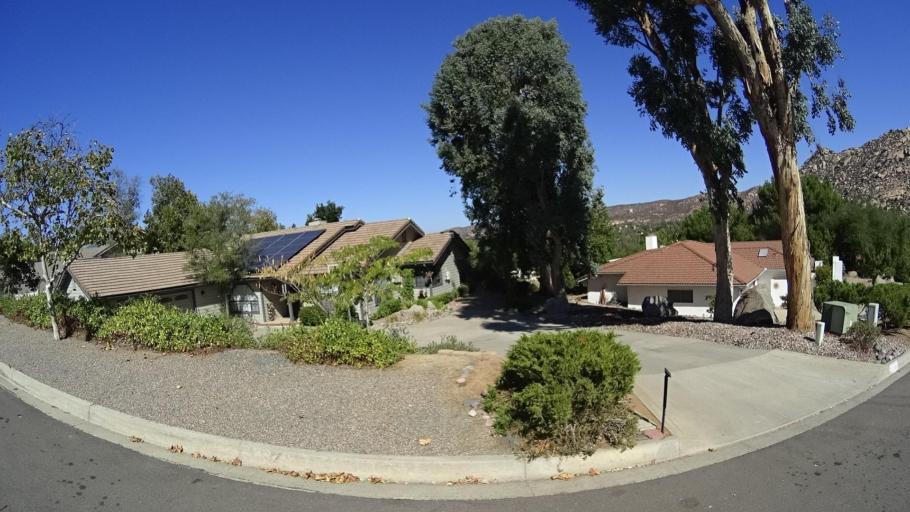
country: US
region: California
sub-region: San Diego County
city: San Diego Country Estates
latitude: 33.0014
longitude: -116.7849
